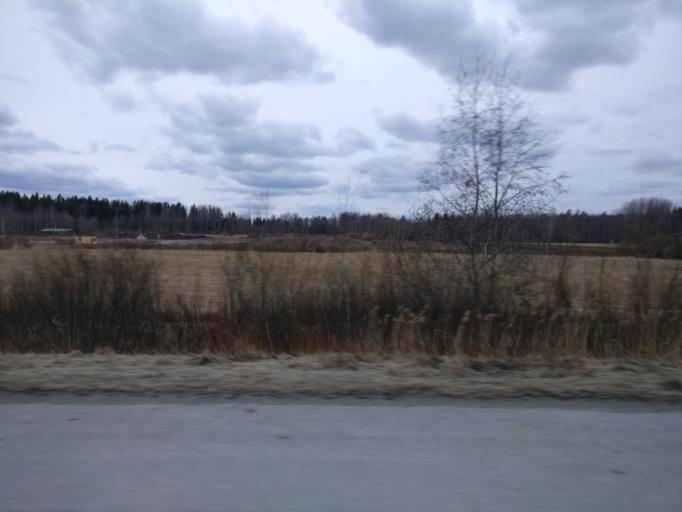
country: FI
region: Haeme
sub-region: Haemeenlinna
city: Parola
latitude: 61.0254
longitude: 24.4009
